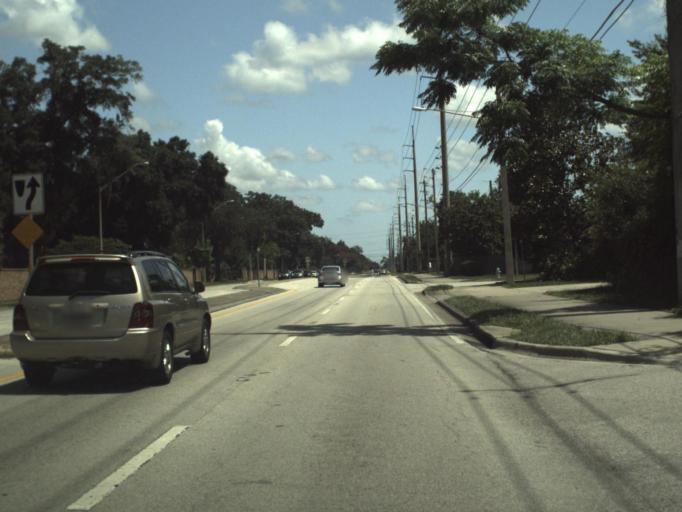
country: US
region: Florida
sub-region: Orange County
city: Conway
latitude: 28.4879
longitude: -81.3307
